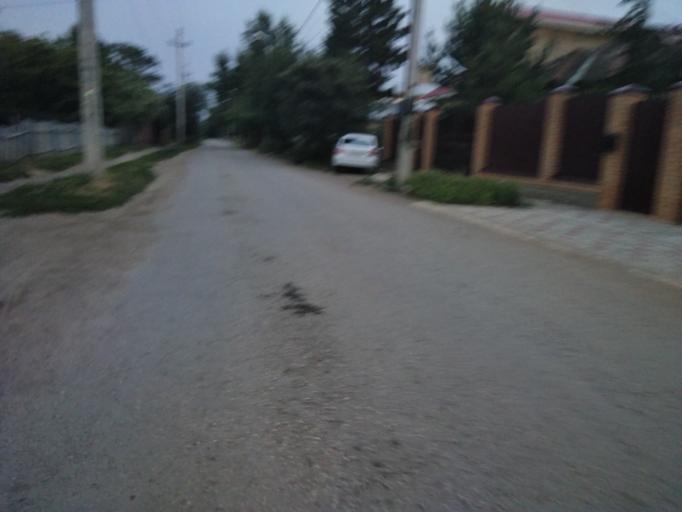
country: RU
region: Tula
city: Lomintsevskiy
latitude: 53.9334
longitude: 37.6222
